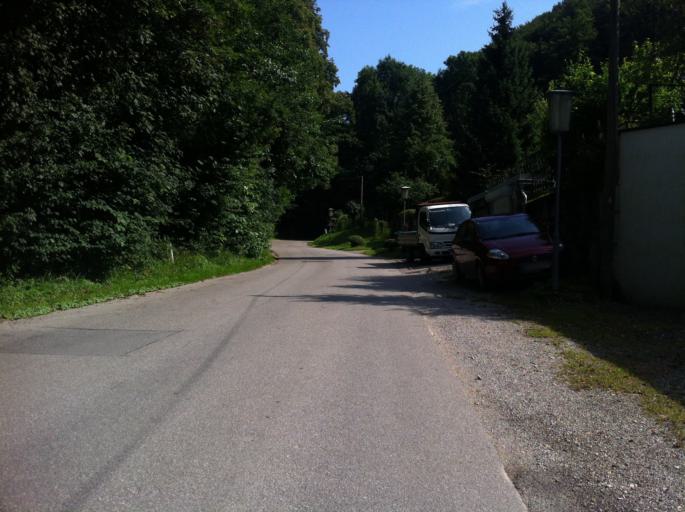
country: AT
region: Lower Austria
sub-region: Politischer Bezirk Wien-Umgebung
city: Purkersdorf
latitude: 48.1895
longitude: 16.1710
